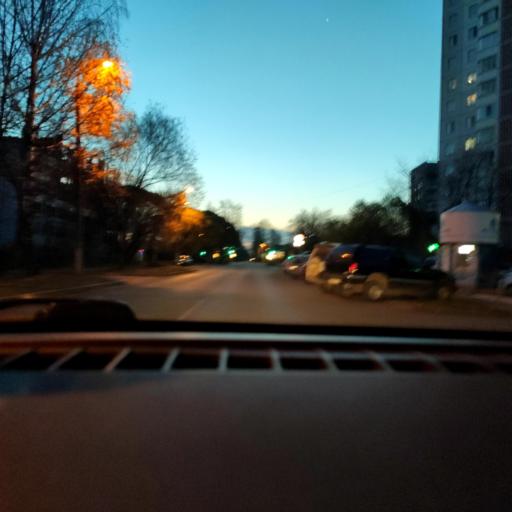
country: RU
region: Perm
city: Perm
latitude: 58.0625
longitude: 56.3592
